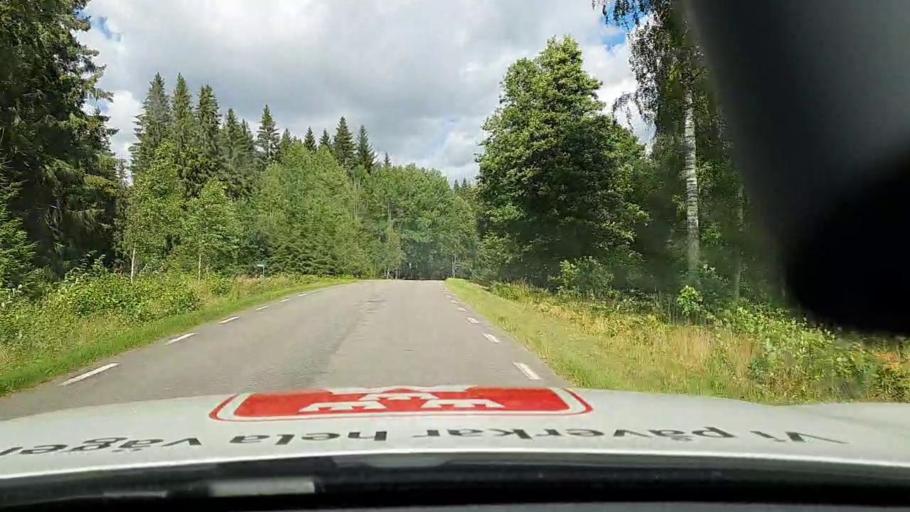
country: SE
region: Vaestra Goetaland
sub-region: Karlsborgs Kommun
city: Molltorp
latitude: 58.6078
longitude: 14.3185
